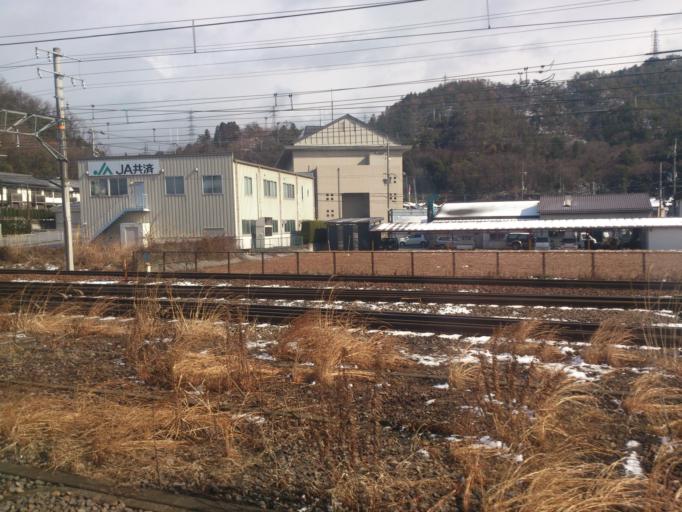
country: JP
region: Shiga Prefecture
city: Nagahama
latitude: 35.3173
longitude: 136.2911
